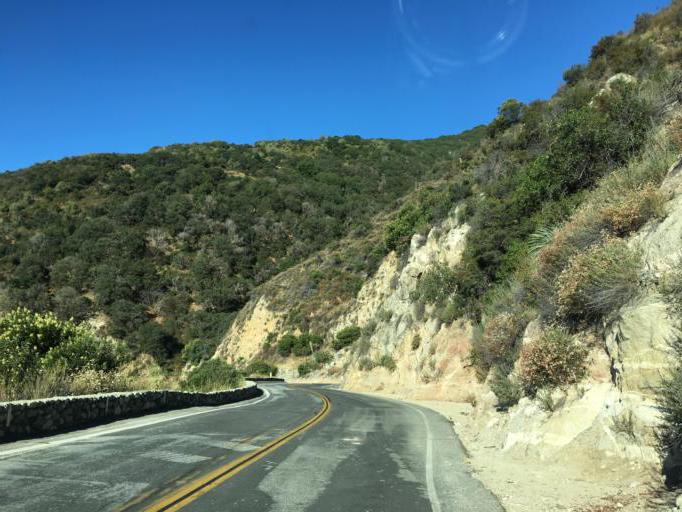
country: US
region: California
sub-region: Los Angeles County
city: Sierra Madre
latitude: 34.1908
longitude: -118.0216
